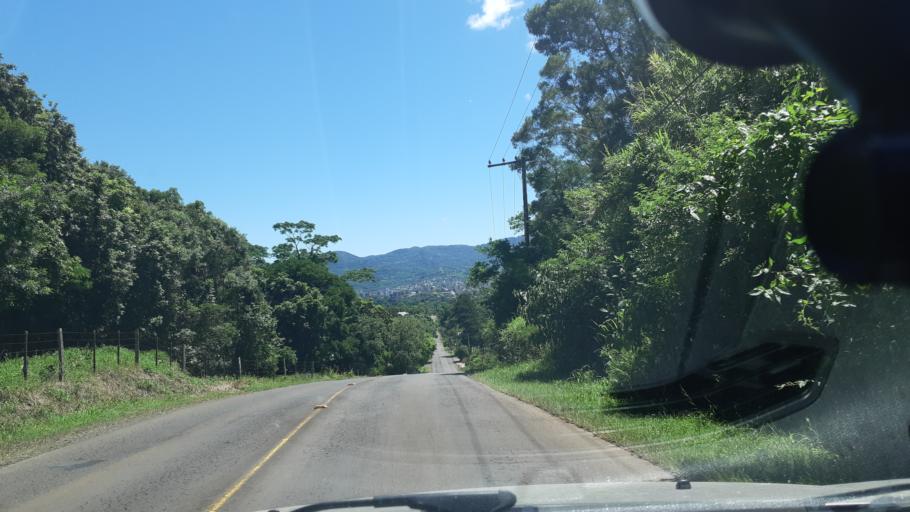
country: BR
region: Rio Grande do Sul
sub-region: Novo Hamburgo
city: Novo Hamburgo
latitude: -29.6192
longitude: -51.0930
